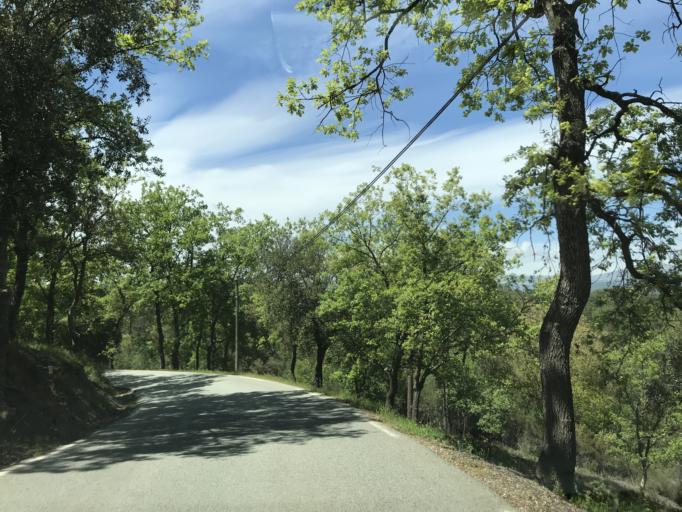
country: FR
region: Provence-Alpes-Cote d'Azur
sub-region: Departement du Var
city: Tanneron
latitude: 43.5848
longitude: 6.8225
